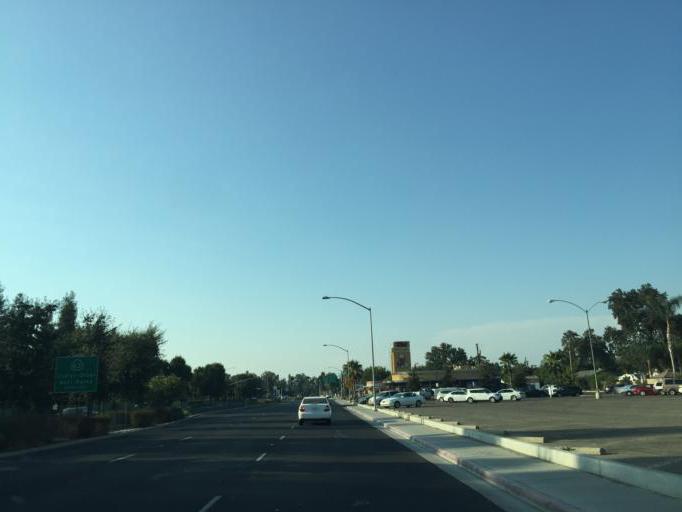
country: US
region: California
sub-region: Tulare County
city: Visalia
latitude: 36.3236
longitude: -119.3138
